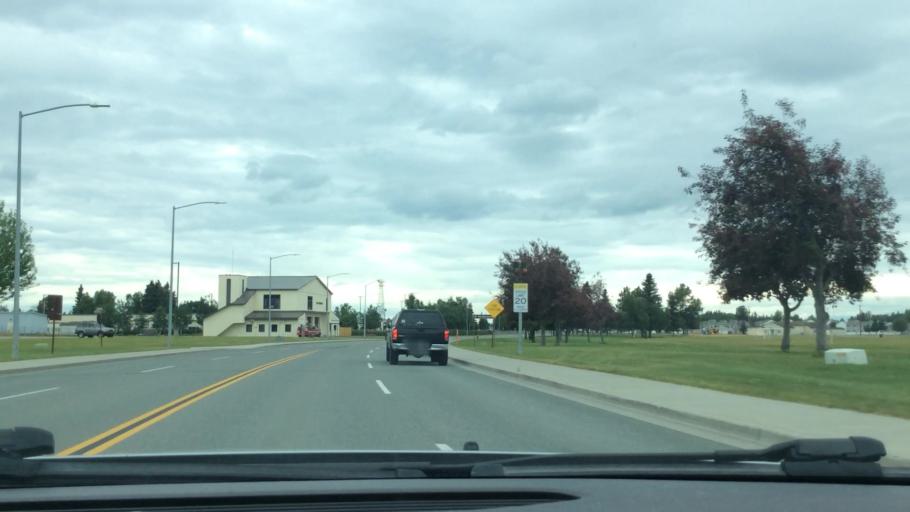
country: US
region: Alaska
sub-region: Anchorage Municipality
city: Anchorage
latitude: 61.2358
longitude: -149.8551
